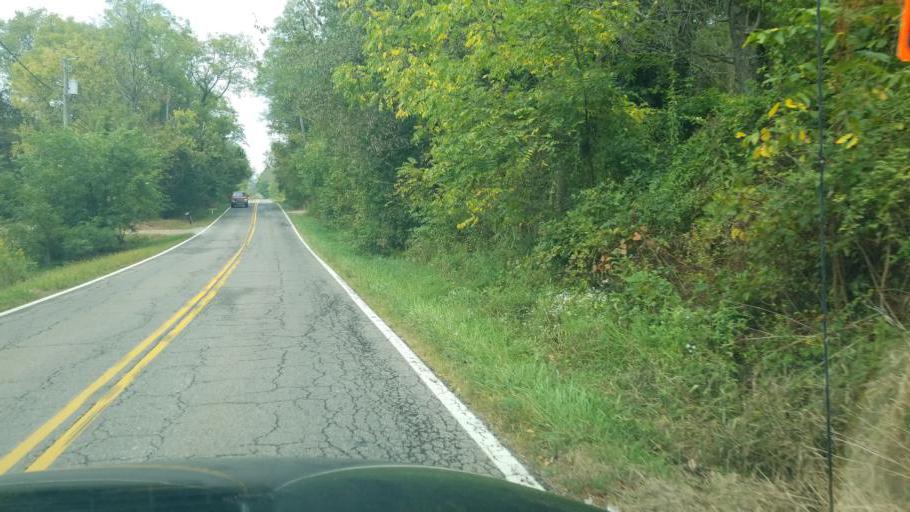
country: US
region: Ohio
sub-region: Perry County
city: Somerset
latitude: 39.9490
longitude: -82.2573
